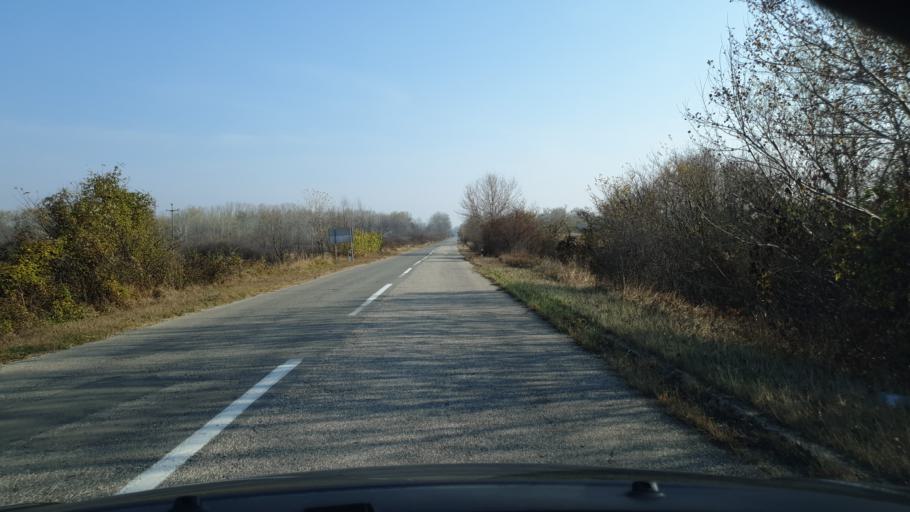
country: BG
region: Vidin
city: Bregovo
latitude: 44.1582
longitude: 22.6073
